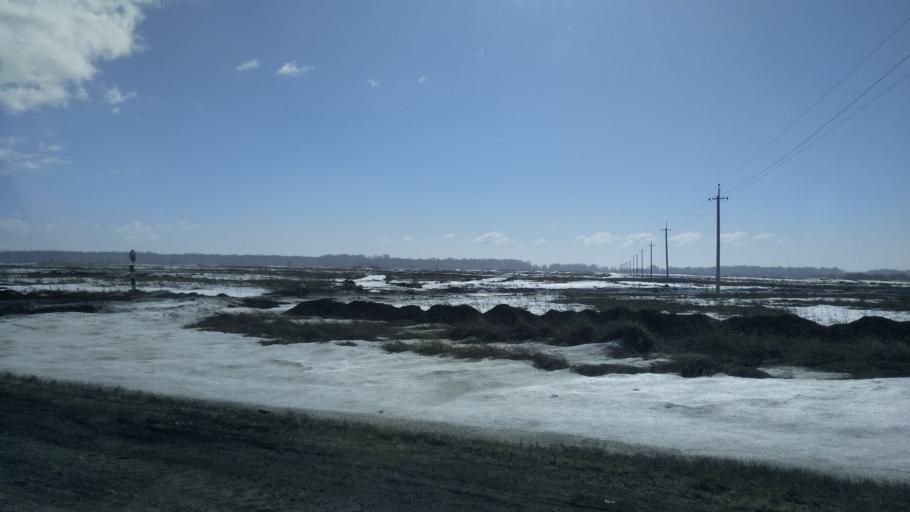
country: RU
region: Kemerovo
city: Yurga
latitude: 55.6836
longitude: 84.9977
